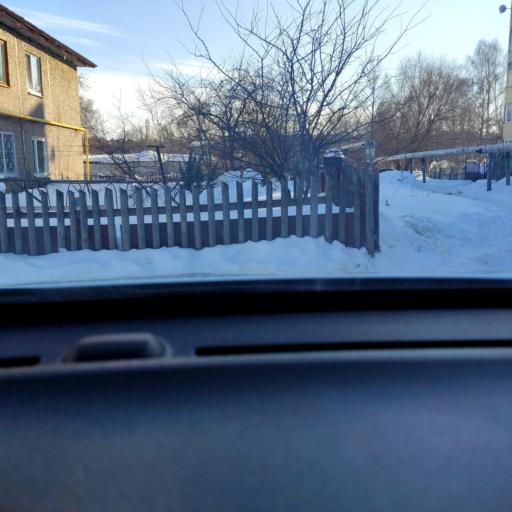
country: RU
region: Tatarstan
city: Osinovo
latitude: 55.8458
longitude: 48.9029
